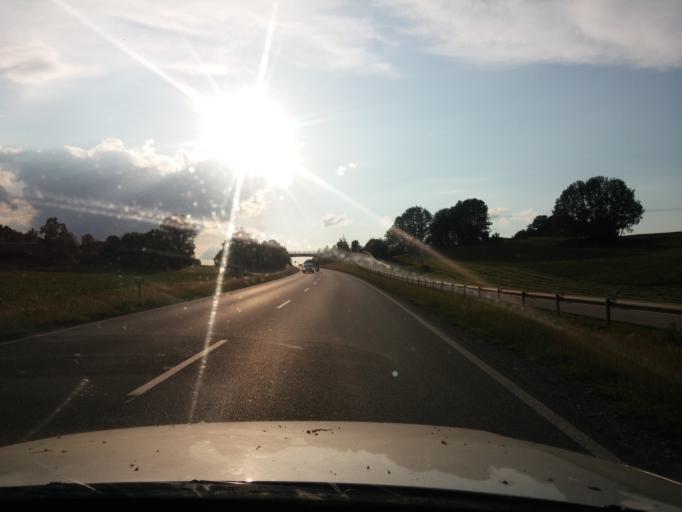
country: DE
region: Bavaria
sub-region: Upper Bavaria
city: Ebersberg
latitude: 48.0644
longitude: 11.9380
